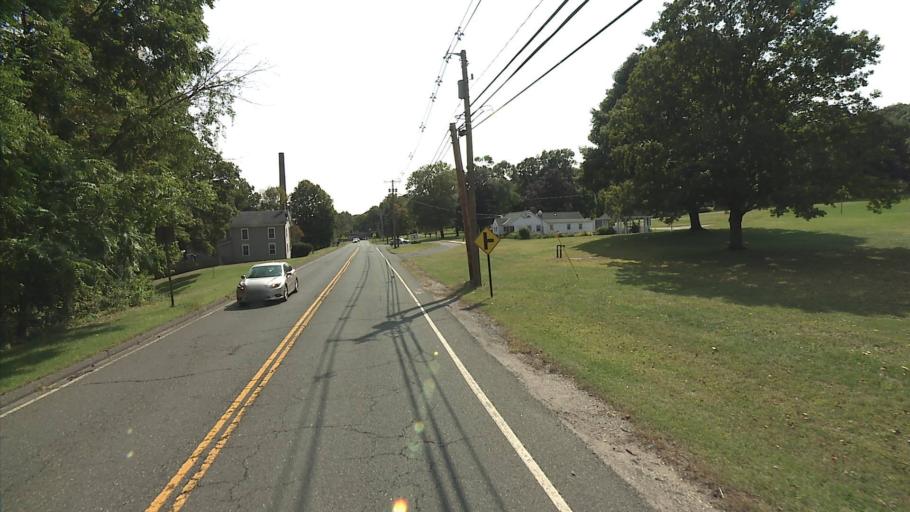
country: US
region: Connecticut
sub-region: New Haven County
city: Heritage Village
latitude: 41.4925
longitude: -73.2608
